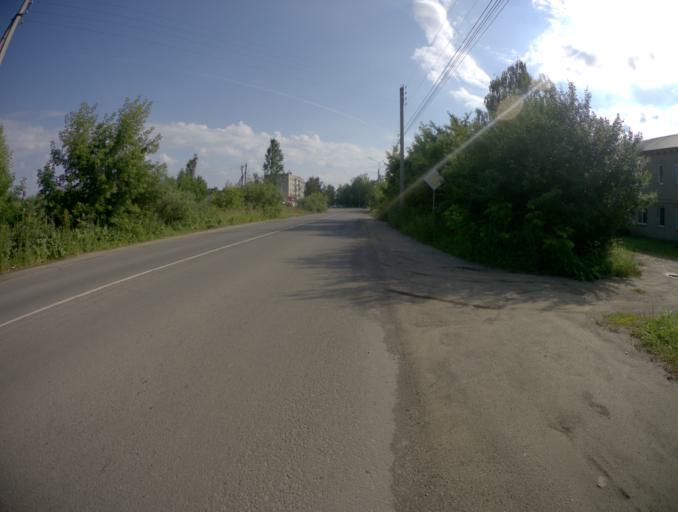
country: RU
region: Vladimir
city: Novovyazniki
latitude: 56.2289
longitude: 42.1954
